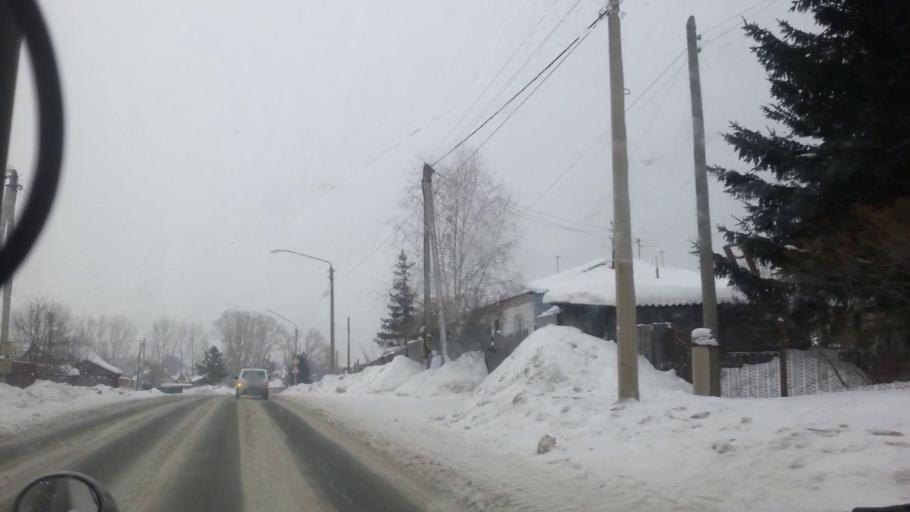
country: RU
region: Altai Krai
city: Vlasikha
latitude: 53.2943
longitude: 83.5754
